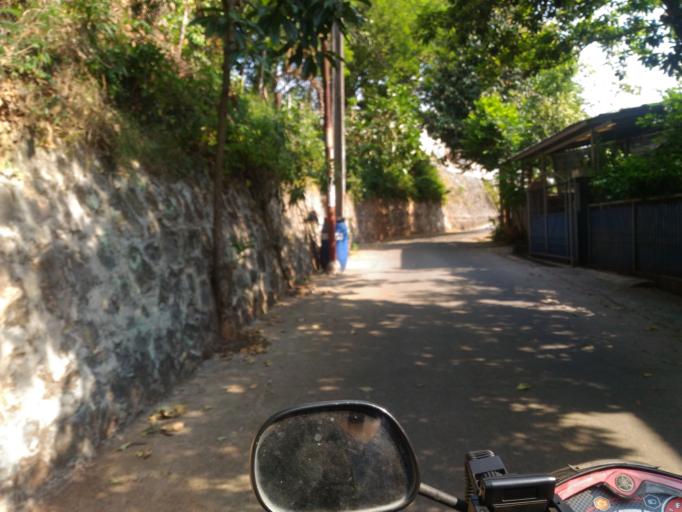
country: ID
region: West Java
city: Depok
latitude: -6.3444
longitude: 106.8403
